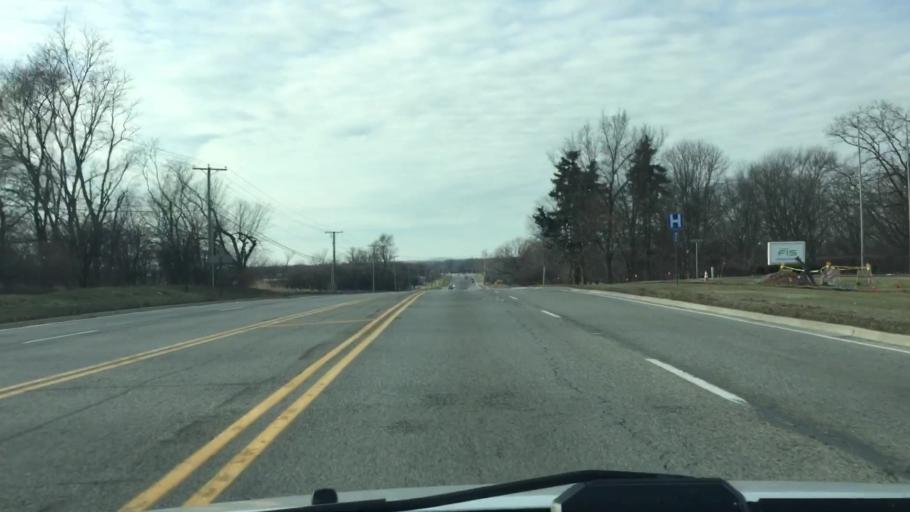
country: US
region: Illinois
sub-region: Kane County
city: Geneva
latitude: 41.8689
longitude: -88.2817
